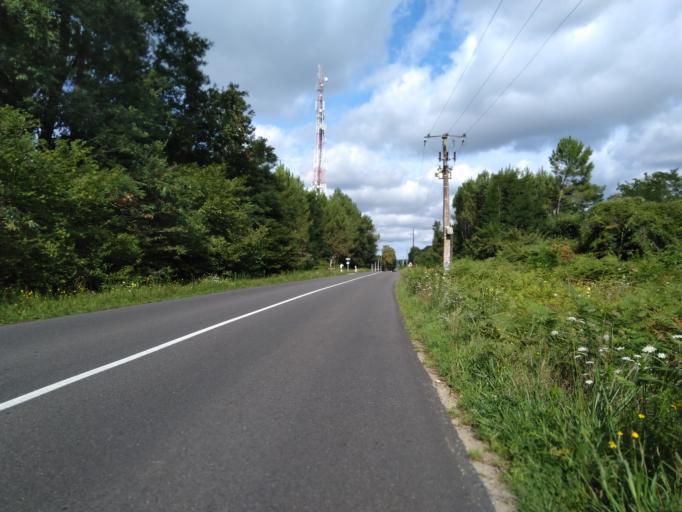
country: FR
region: Aquitaine
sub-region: Departement des Landes
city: Mees
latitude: 43.7333
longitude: -1.1049
